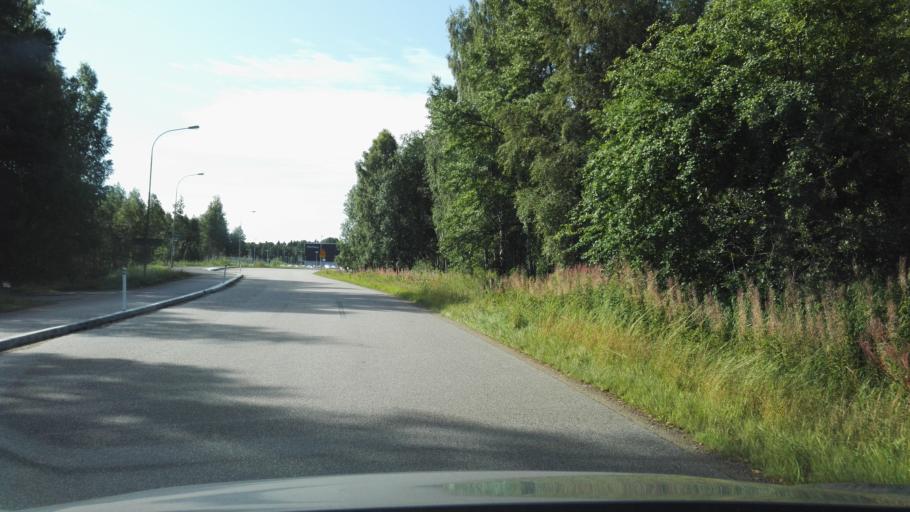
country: SE
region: Kronoberg
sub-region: Vaxjo Kommun
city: Vaexjoe
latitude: 56.8797
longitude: 14.7459
